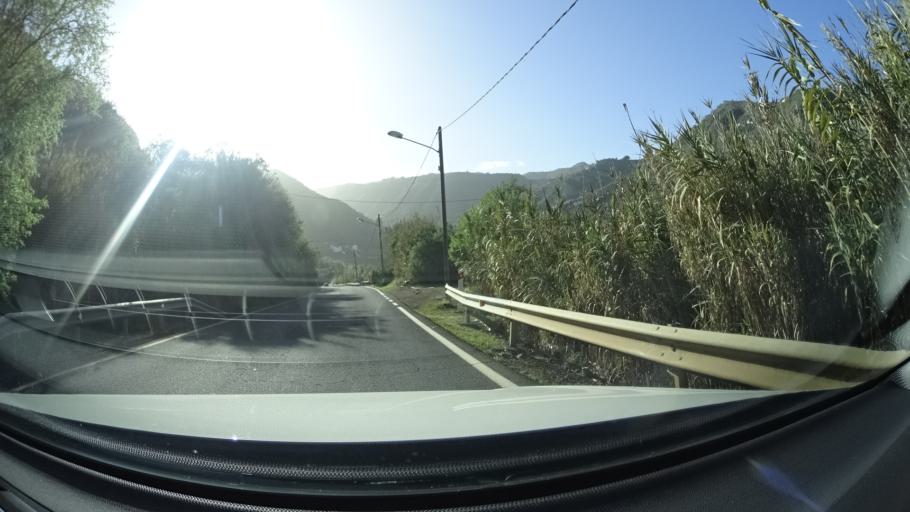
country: ES
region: Canary Islands
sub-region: Provincia de Las Palmas
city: Vega de San Mateo
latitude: 28.0173
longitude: -15.5489
